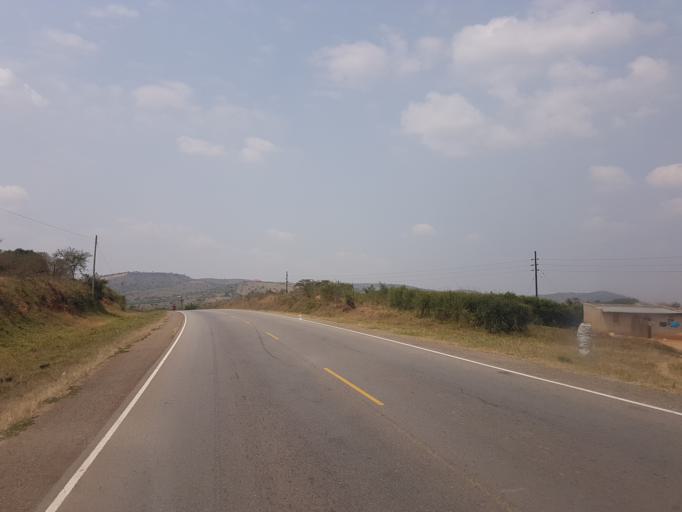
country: UG
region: Western Region
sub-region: Mbarara District
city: Mbarara
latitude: -0.5095
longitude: 30.8387
